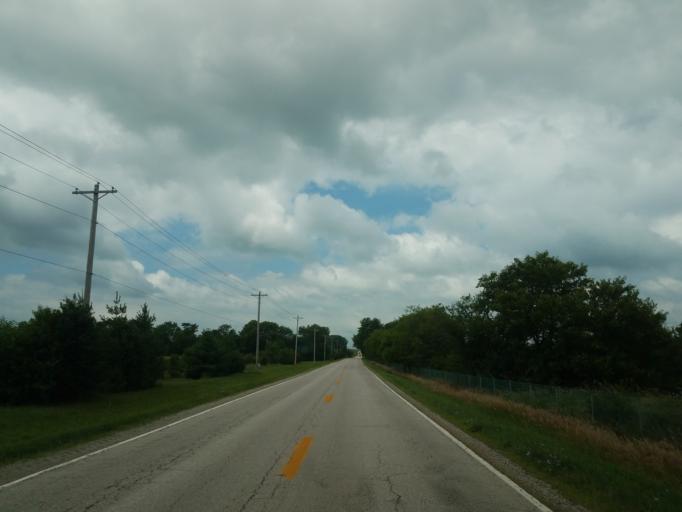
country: US
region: Illinois
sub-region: McLean County
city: Bloomington
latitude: 40.4586
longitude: -89.0382
